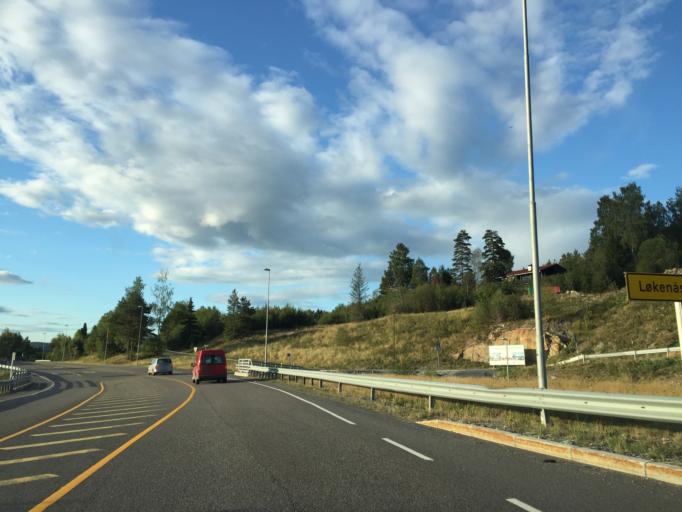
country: NO
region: Akershus
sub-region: Fet
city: Fetsund
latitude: 59.9175
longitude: 11.1841
